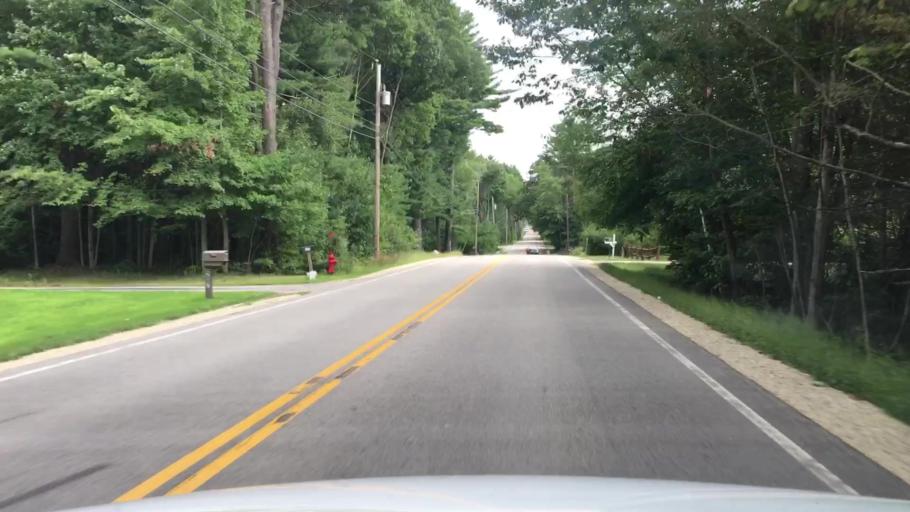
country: US
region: New Hampshire
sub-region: Strafford County
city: Somersworth
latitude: 43.2419
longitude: -70.9080
